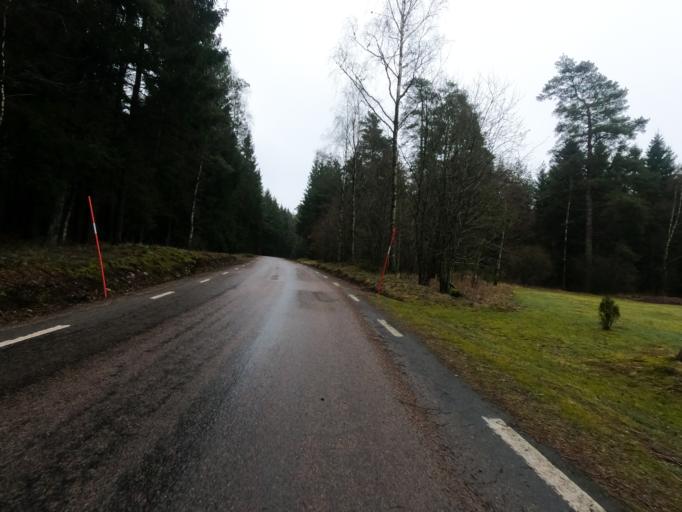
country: SE
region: Halland
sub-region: Hylte Kommun
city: Hyltebruk
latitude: 56.7949
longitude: 13.2022
